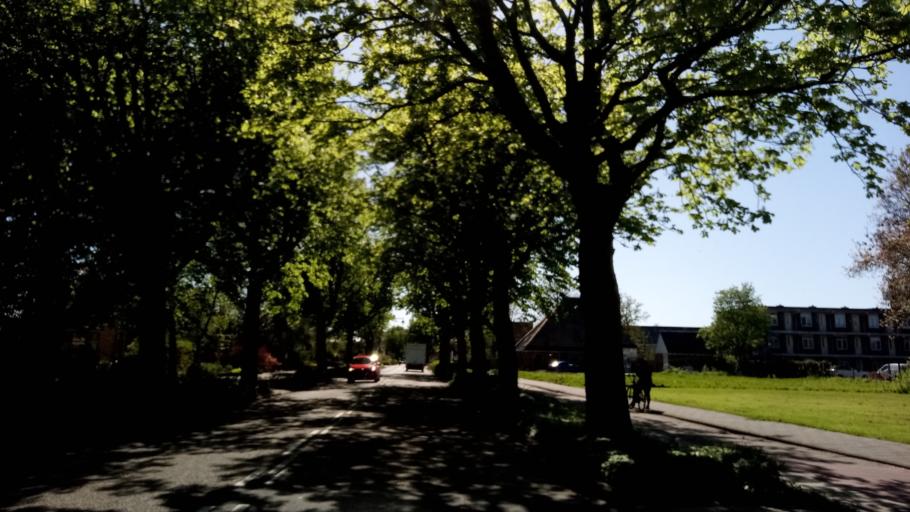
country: NL
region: North Holland
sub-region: Gemeente Heerhugowaard
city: Heerhugowaard
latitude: 52.6665
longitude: 4.8395
